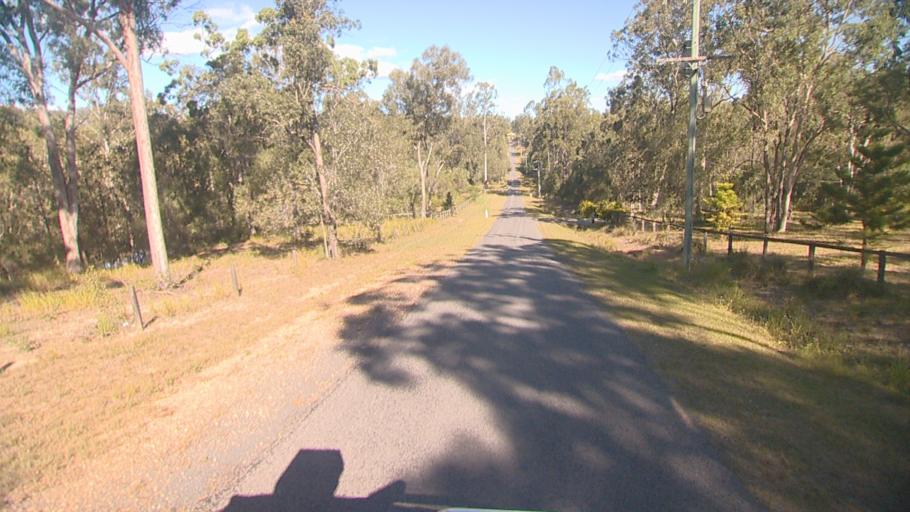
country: AU
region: Queensland
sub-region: Logan
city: Chambers Flat
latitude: -27.8163
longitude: 153.0773
